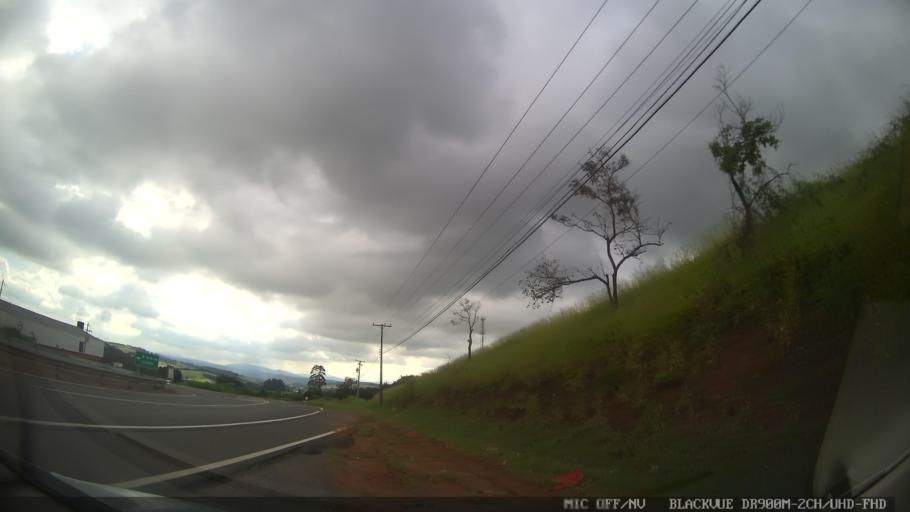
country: BR
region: Sao Paulo
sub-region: Itatiba
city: Itatiba
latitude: -22.9780
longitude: -46.7698
